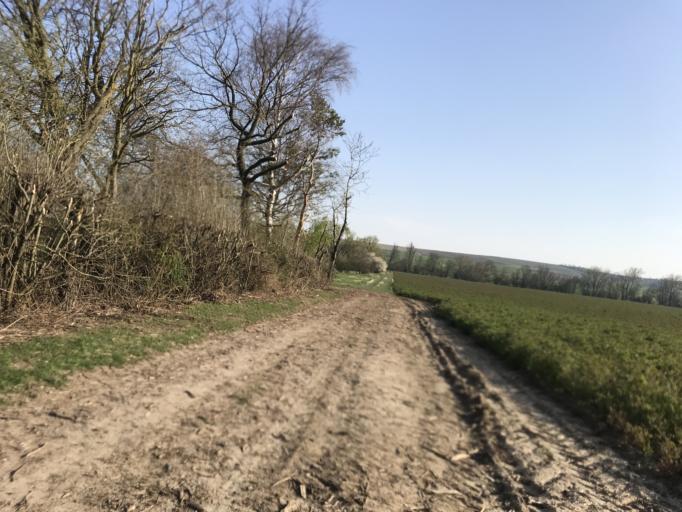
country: DE
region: Rheinland-Pfalz
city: Essenheim
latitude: 49.9185
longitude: 8.1687
